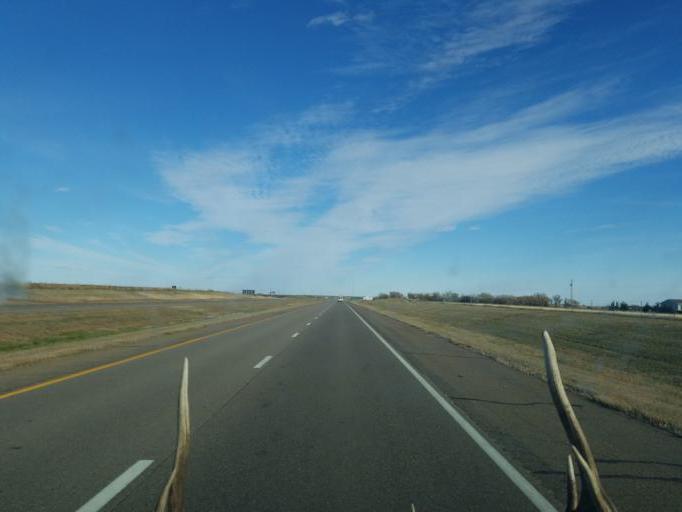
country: US
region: Kansas
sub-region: Ellis County
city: Hays
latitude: 38.8779
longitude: -99.2551
